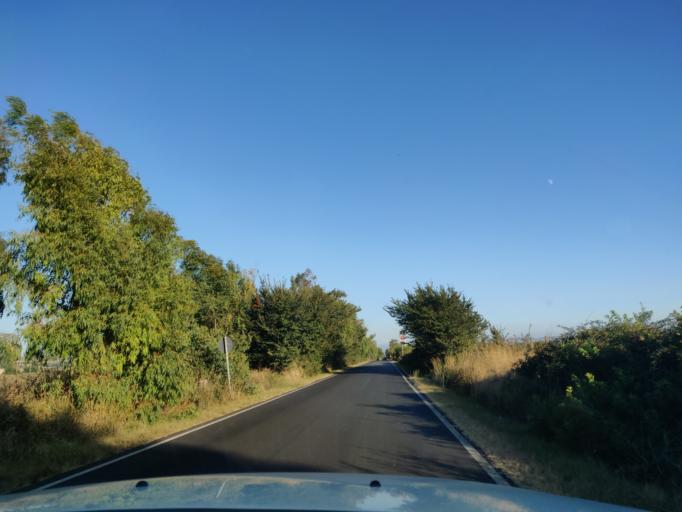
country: IT
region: Latium
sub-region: Provincia di Viterbo
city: Tarquinia
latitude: 42.2751
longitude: 11.6826
